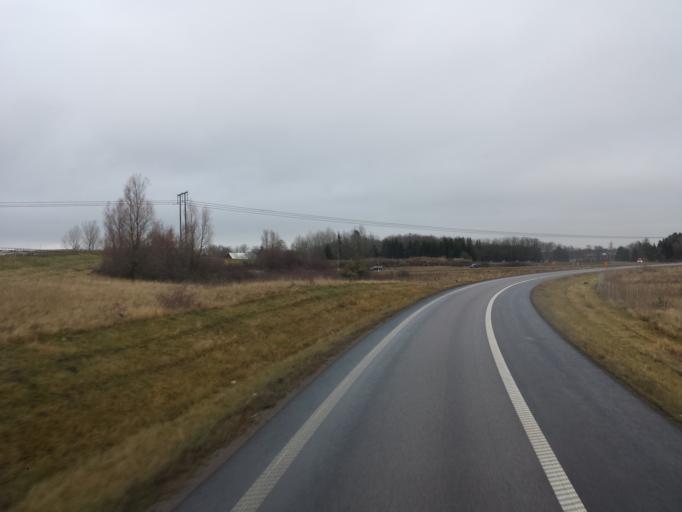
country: SE
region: OEstergoetland
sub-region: Linkopings Kommun
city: Ekangen
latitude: 58.4311
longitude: 15.6703
